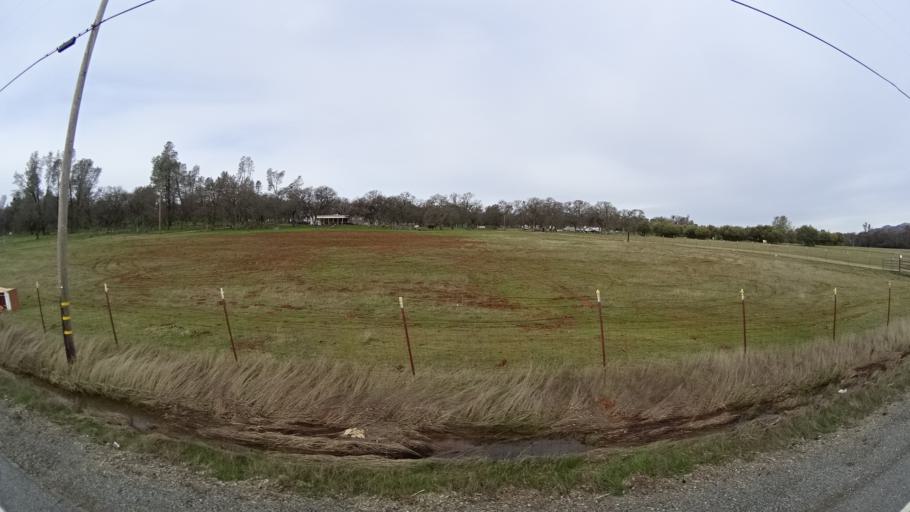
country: US
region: California
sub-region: Yuba County
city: Loma Rica
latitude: 39.3843
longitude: -121.4091
